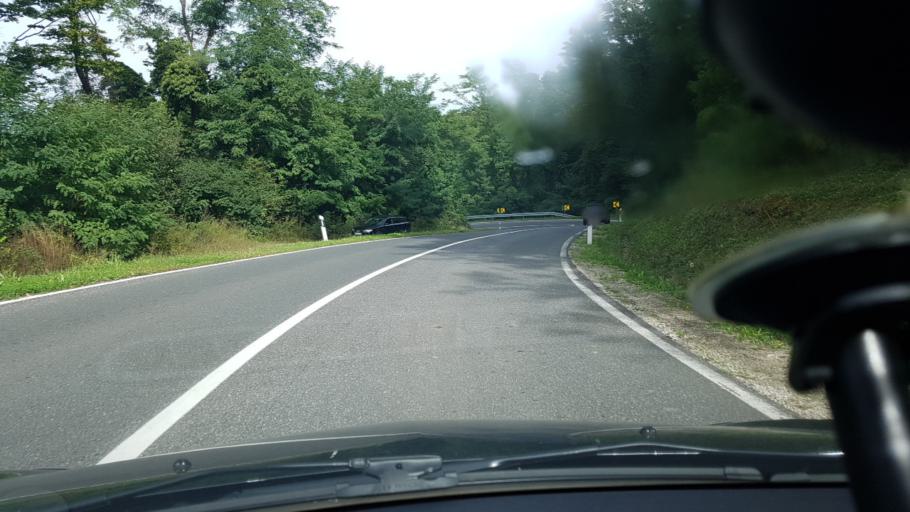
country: HR
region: Varazdinska
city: Ljubescica
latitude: 46.1328
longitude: 16.3608
